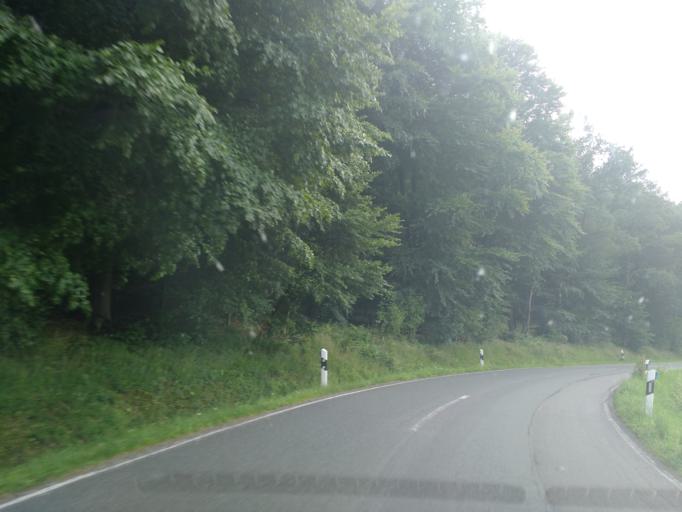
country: DE
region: North Rhine-Westphalia
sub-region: Regierungsbezirk Detmold
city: Dorentrup
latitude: 52.0459
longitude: 9.0304
